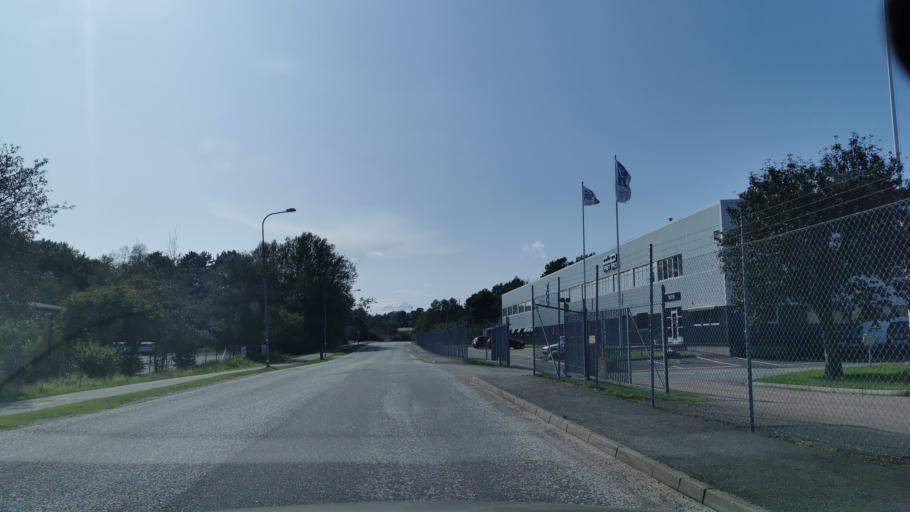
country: SE
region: Vaestra Goetaland
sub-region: Goteborg
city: Majorna
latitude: 57.6447
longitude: 11.9237
